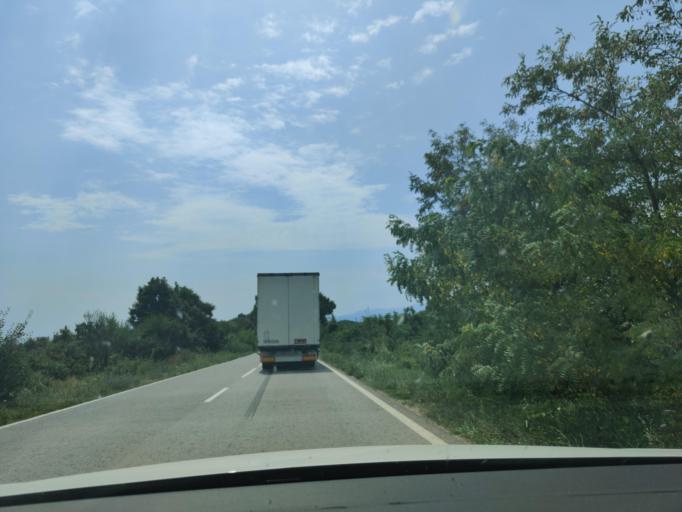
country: BG
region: Vidin
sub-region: Obshtina Ruzhintsi
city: Ruzhintsi
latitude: 43.6429
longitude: 22.7954
